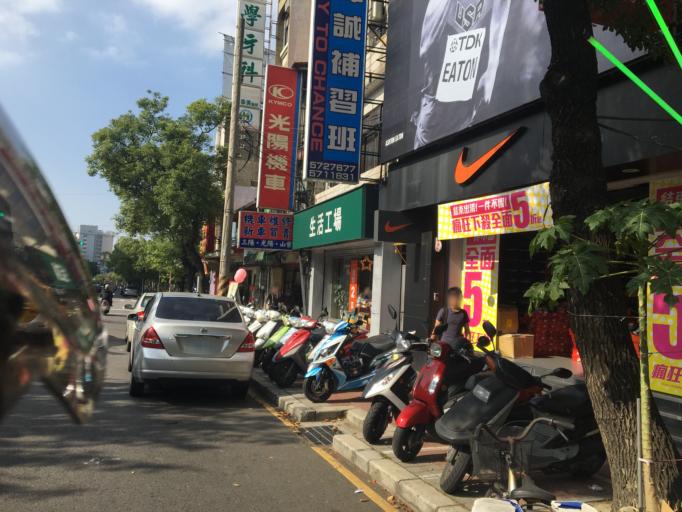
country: TW
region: Taiwan
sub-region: Hsinchu
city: Hsinchu
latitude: 24.7973
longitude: 120.9963
